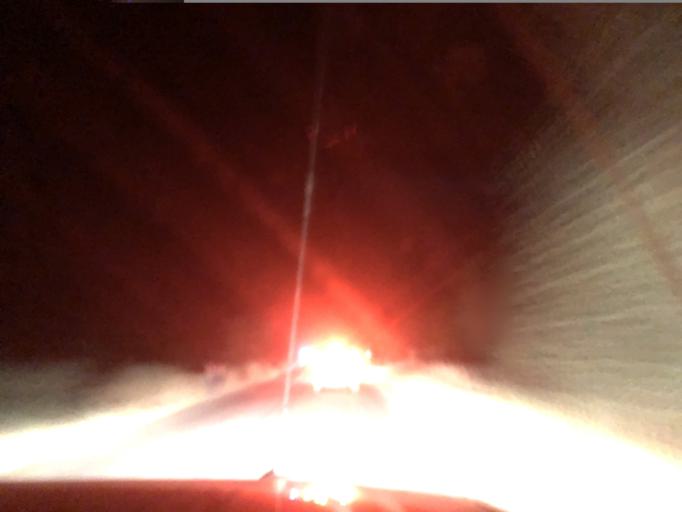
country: CM
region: Far North
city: Kousseri
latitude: 11.9439
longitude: 15.1669
